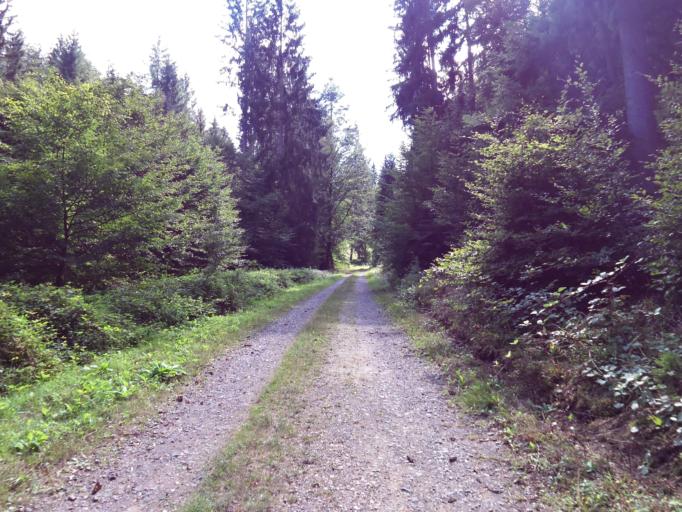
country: DE
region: Rheinland-Pfalz
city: Weidenthal
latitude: 49.4063
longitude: 7.9890
